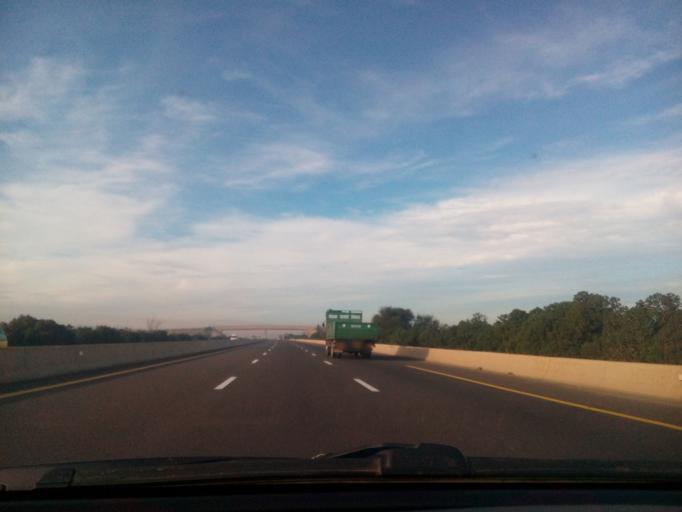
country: DZ
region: Mascara
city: Sig
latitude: 35.5900
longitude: -0.0758
